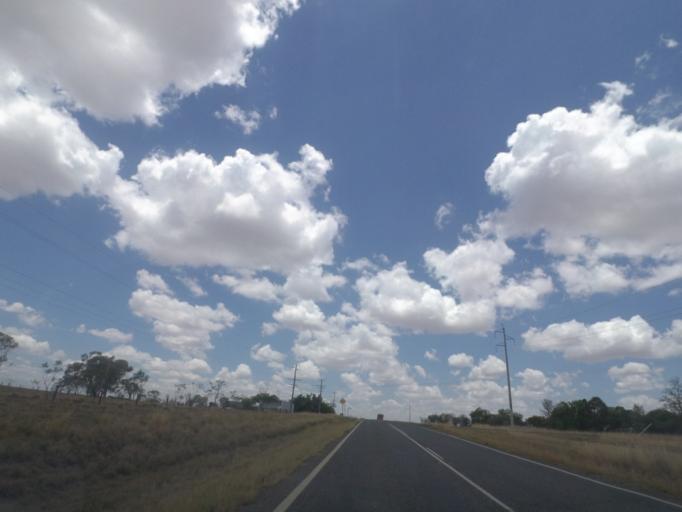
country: AU
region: Queensland
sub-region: Toowoomba
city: Top Camp
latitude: -27.8833
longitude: 151.9706
